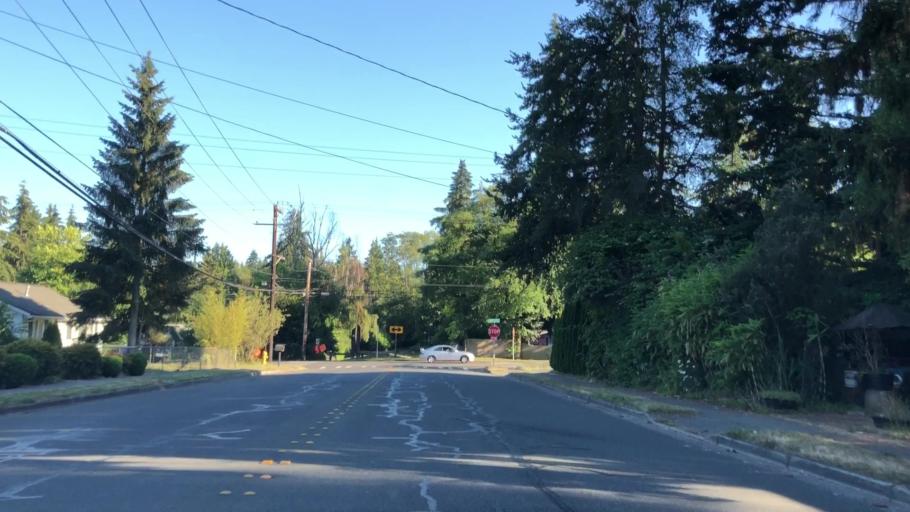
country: US
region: Washington
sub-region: Snohomish County
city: Lynnwood
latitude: 47.8108
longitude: -122.3141
